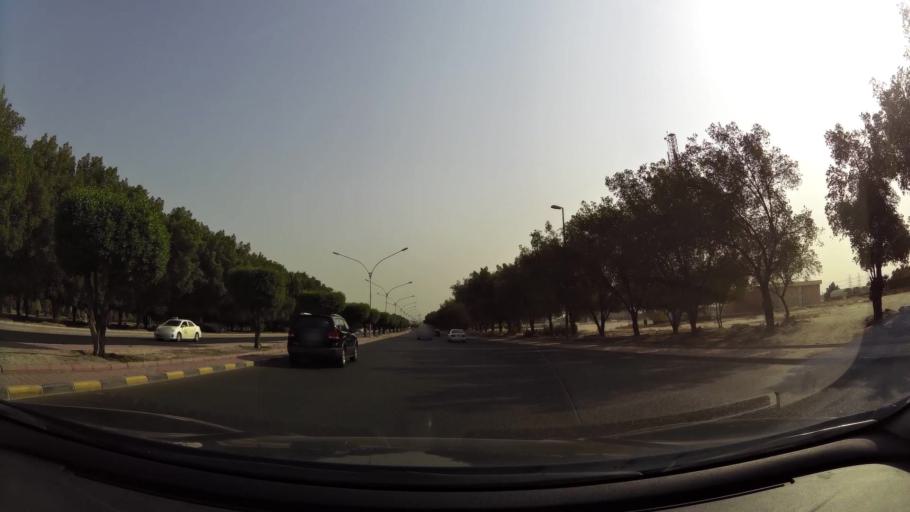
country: KW
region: Mubarak al Kabir
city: Sabah as Salim
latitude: 29.2730
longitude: 48.0645
